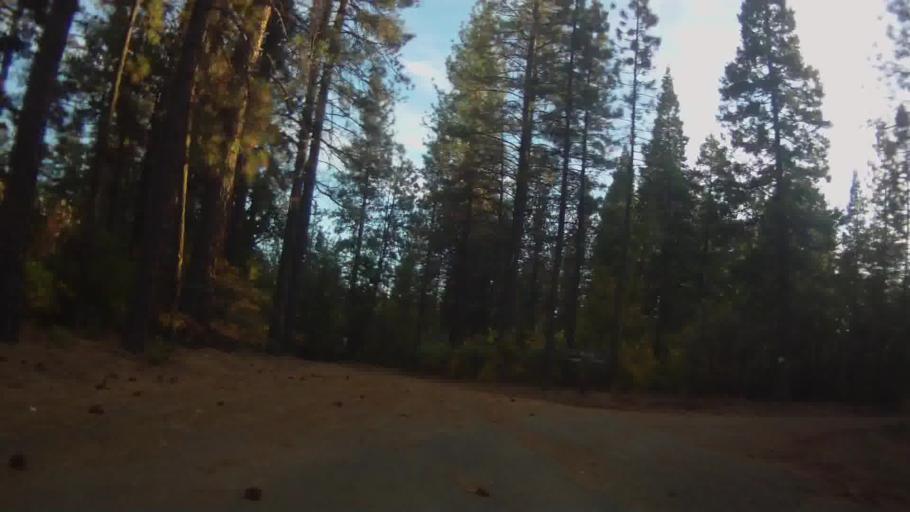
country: US
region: California
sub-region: Shasta County
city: Shingletown
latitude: 40.6238
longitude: -121.8571
